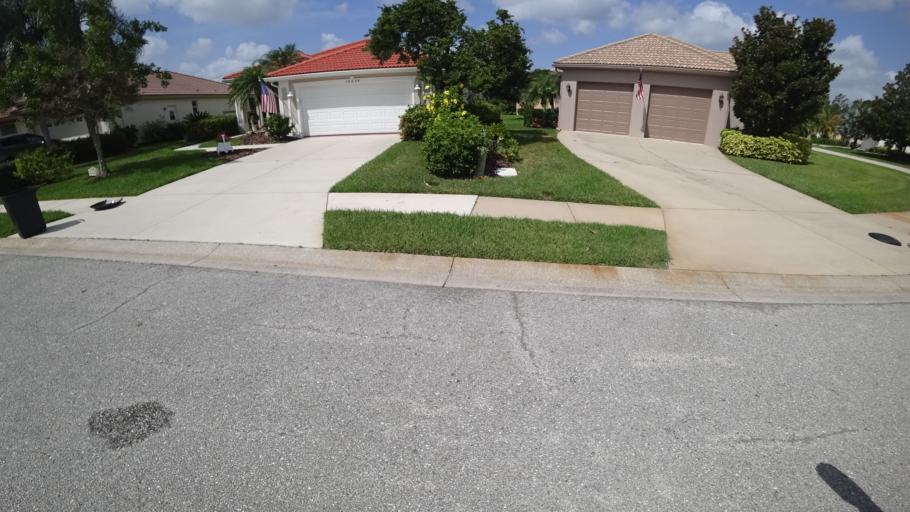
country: US
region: Florida
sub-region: Sarasota County
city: The Meadows
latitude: 27.4096
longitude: -82.4376
